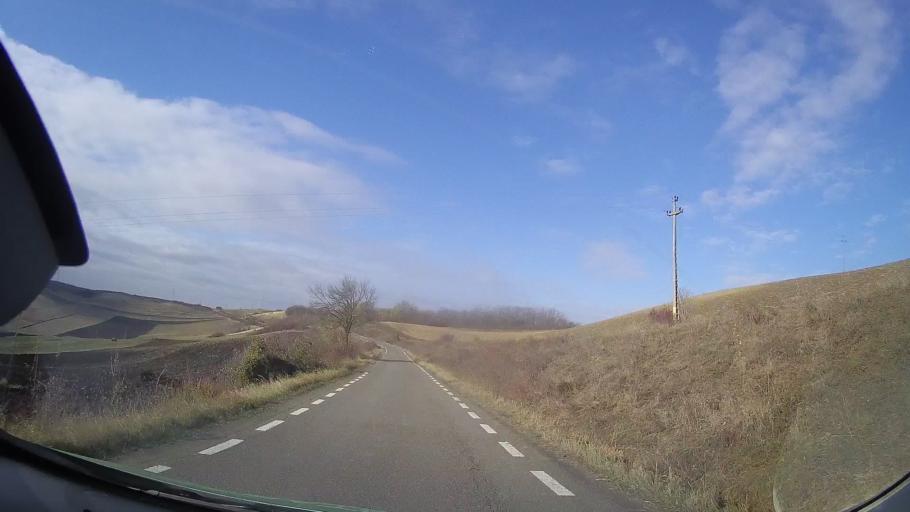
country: RO
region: Mures
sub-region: Comuna Papiu Ilarian
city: Papiu Ilarian
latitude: 46.5594
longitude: 24.1736
